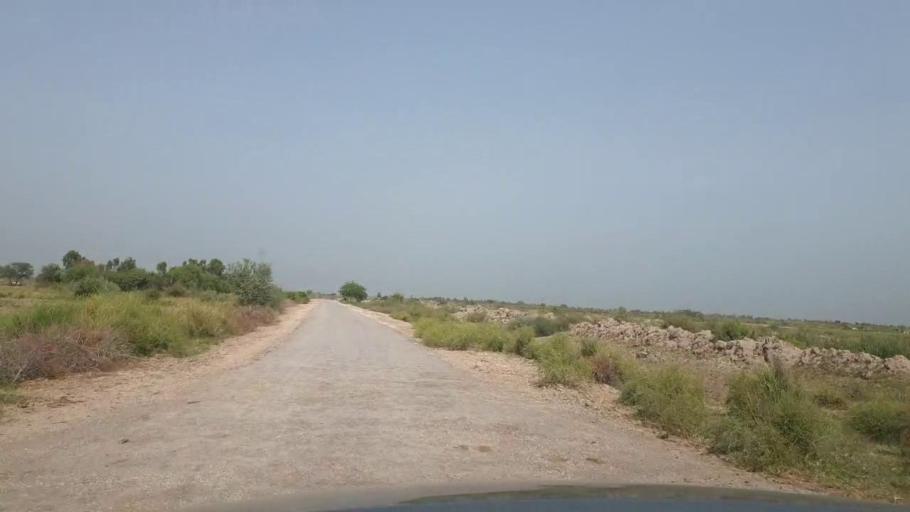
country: PK
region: Sindh
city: Madeji
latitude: 27.8272
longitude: 68.4498
